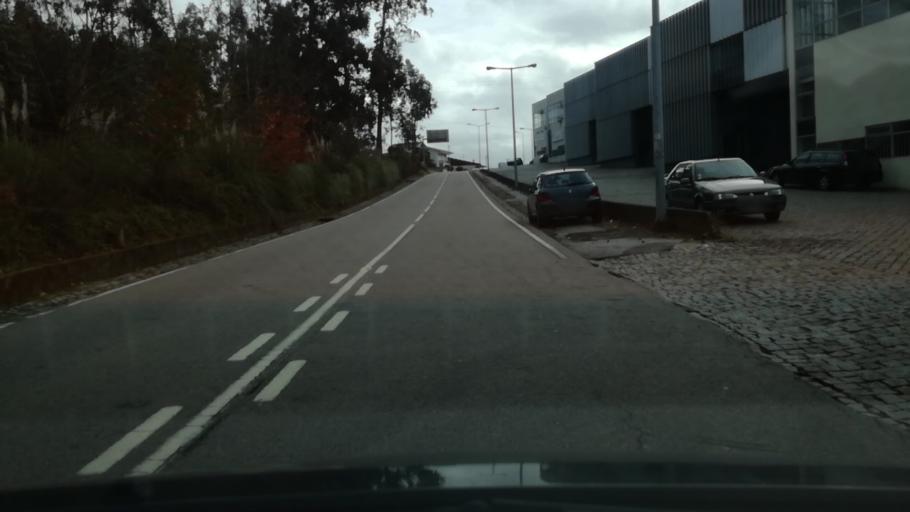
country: PT
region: Porto
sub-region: Maia
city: Maia
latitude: 41.2433
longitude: -8.6354
